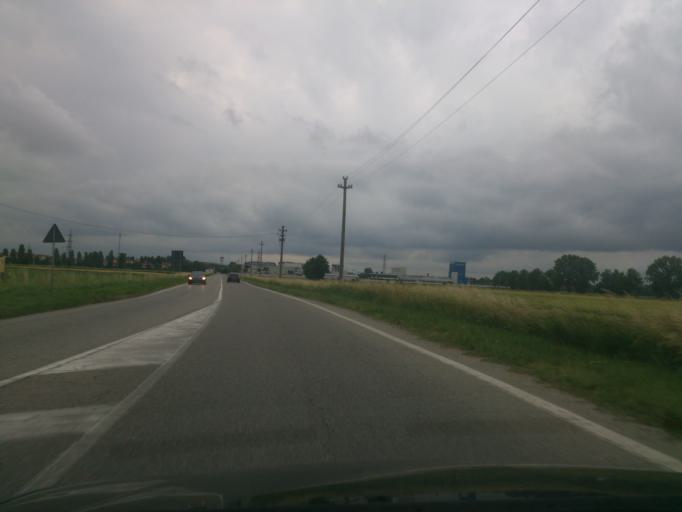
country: IT
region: Lombardy
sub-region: Citta metropolitana di Milano
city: Triginto
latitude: 45.4143
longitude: 9.3150
